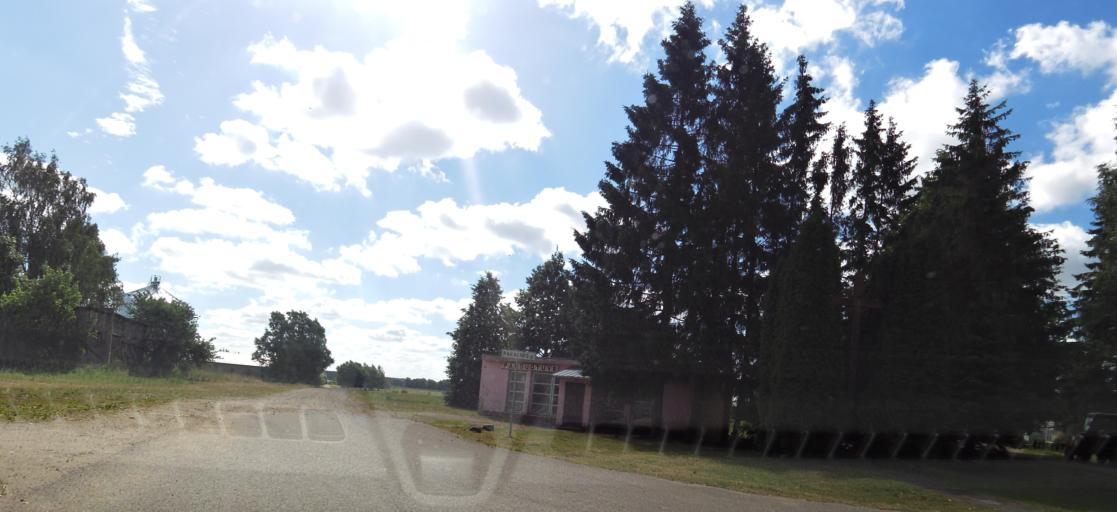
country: LT
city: Vabalninkas
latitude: 56.0623
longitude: 24.8315
